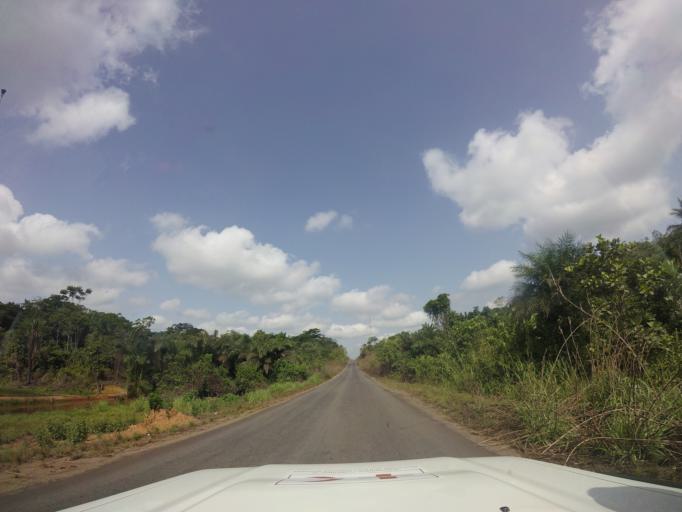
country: LR
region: Bomi
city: Tubmanburg
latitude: 6.6901
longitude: -10.8846
